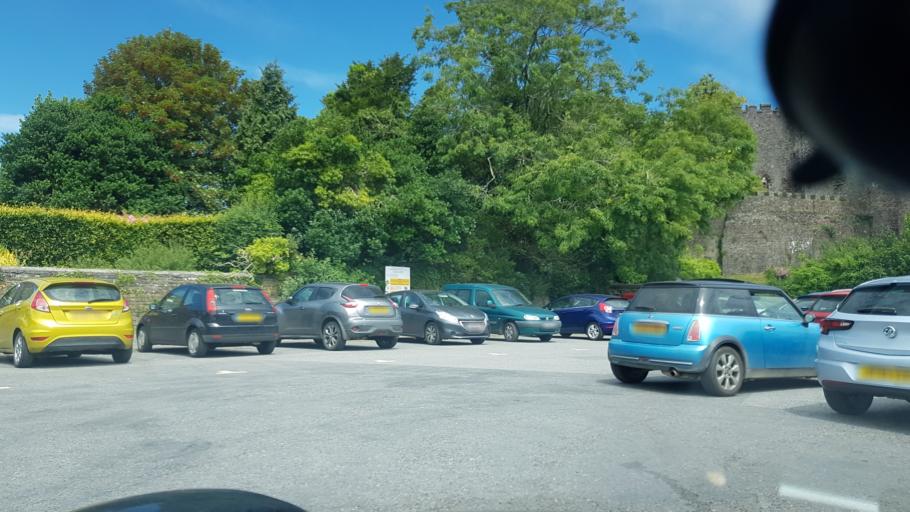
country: GB
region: Wales
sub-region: Carmarthenshire
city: Saint Clears
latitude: 51.7689
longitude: -4.4633
